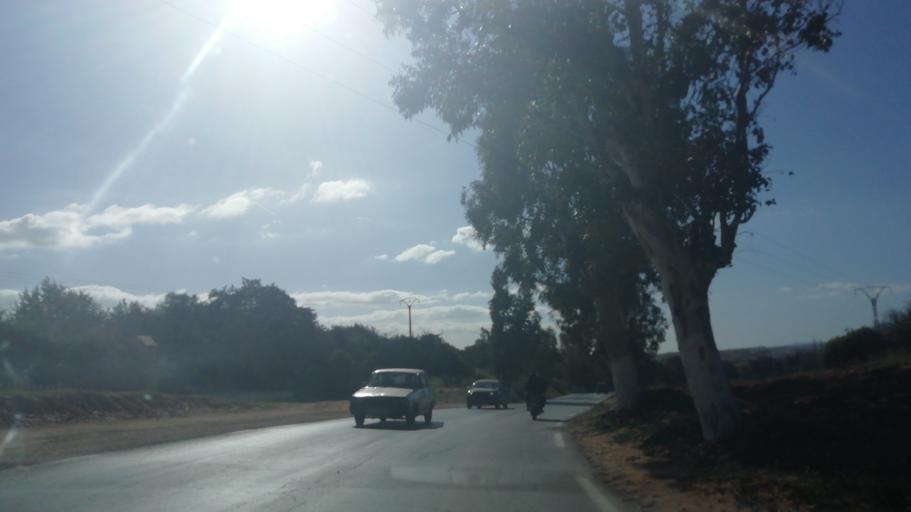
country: DZ
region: Mostaganem
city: Mostaganem
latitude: 35.9991
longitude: 0.3258
